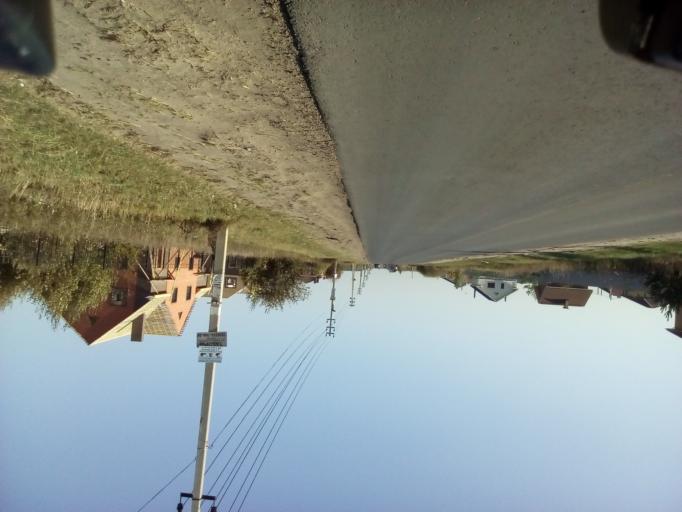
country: RU
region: Moskovskaya
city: Ramenskoye
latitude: 55.5652
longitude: 38.3012
